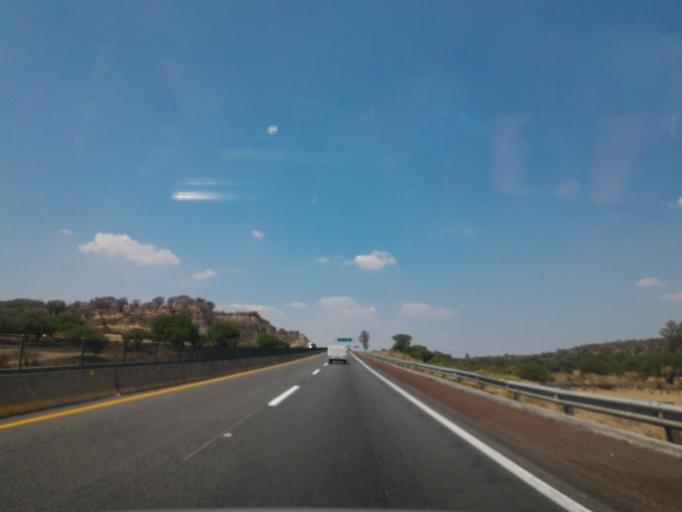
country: MX
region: Jalisco
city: Jalostotitlan
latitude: 21.1083
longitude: -102.4673
